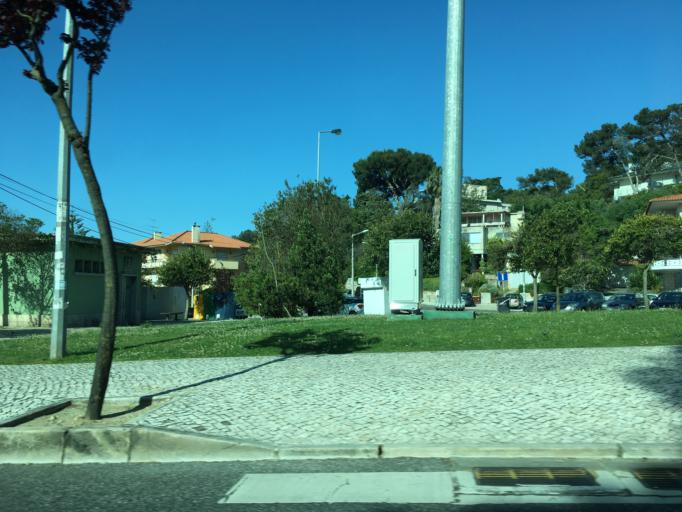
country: PT
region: Lisbon
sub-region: Cascais
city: Monte Estoril
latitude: 38.7062
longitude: -9.4181
